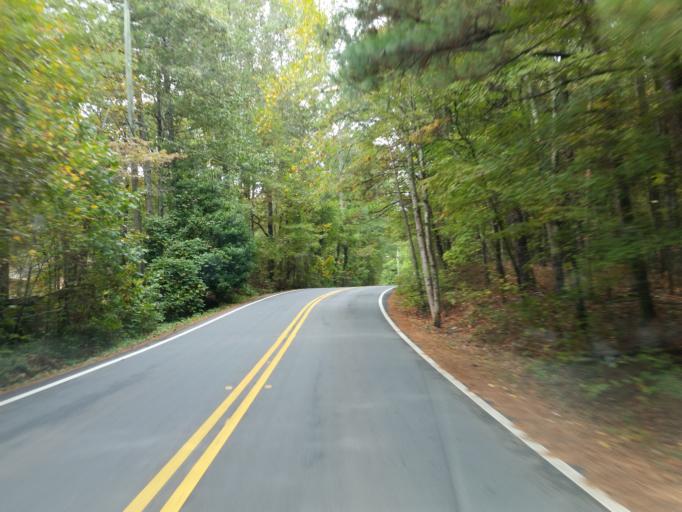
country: US
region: Georgia
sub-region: Fulton County
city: Roswell
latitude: 34.0028
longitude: -84.4487
